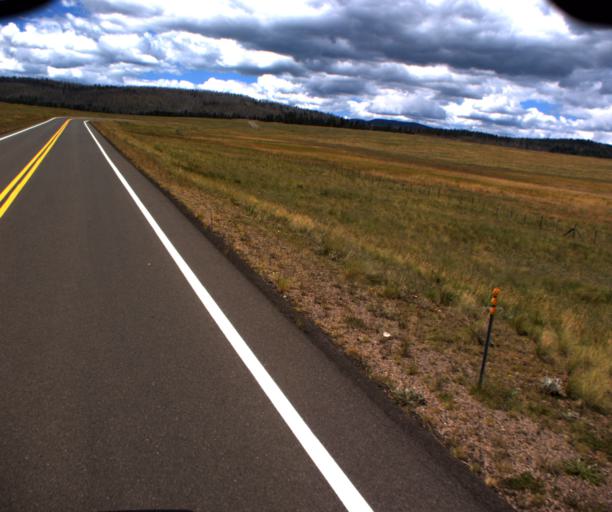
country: US
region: Arizona
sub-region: Apache County
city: Eagar
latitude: 33.9210
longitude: -109.4335
